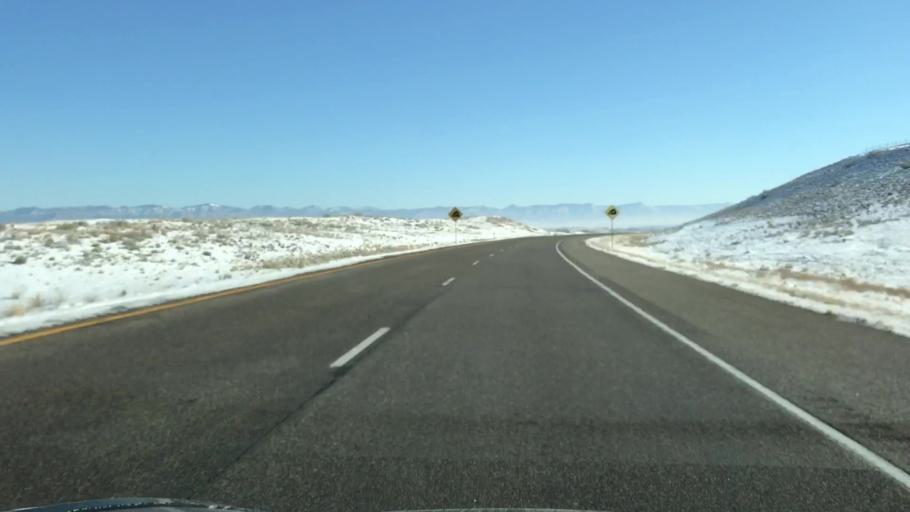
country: US
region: Colorado
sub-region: Mesa County
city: Loma
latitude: 39.2300
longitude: -108.9130
